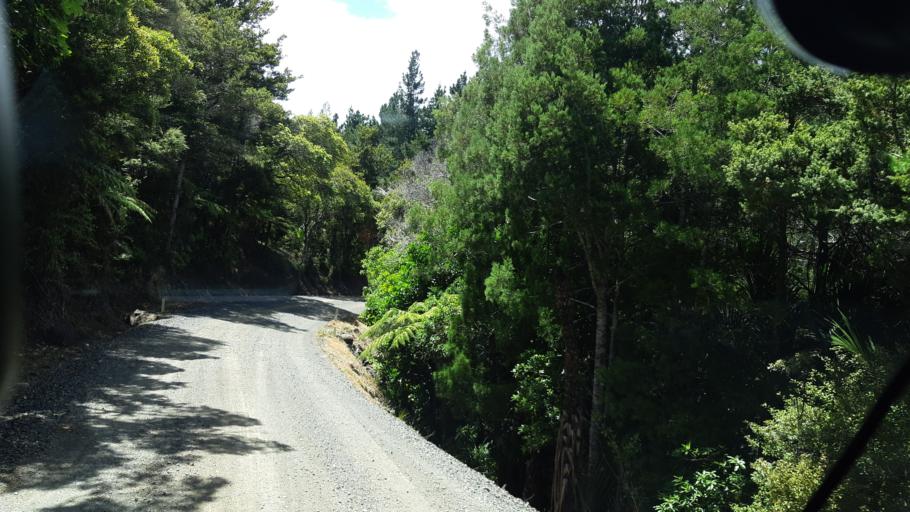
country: NZ
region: Northland
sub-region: Far North District
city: Kaitaia
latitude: -35.2290
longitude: 173.3078
